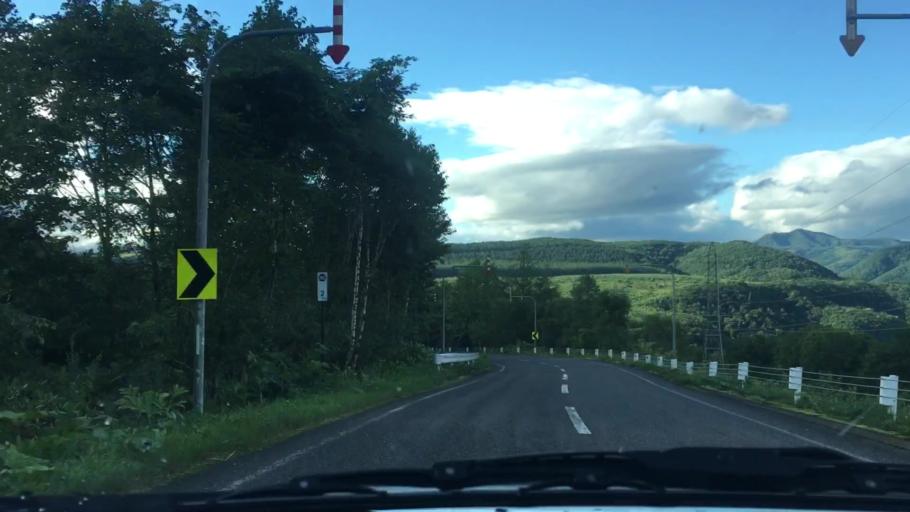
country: JP
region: Hokkaido
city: Otofuke
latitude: 43.1743
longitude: 142.9295
